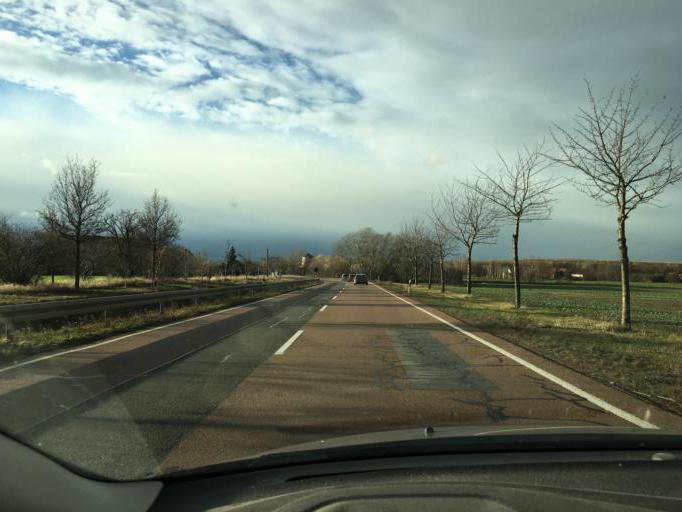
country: DE
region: Saxony-Anhalt
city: Geusa
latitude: 51.3725
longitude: 11.9469
